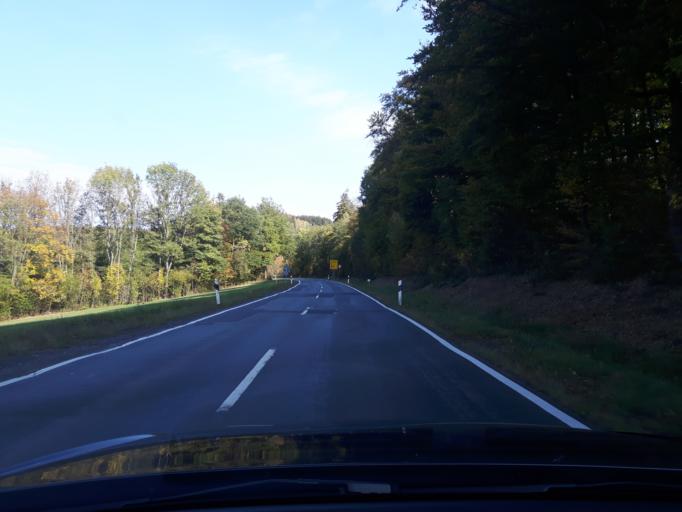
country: DE
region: Hesse
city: Hatzfeld
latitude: 50.9818
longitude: 8.5703
